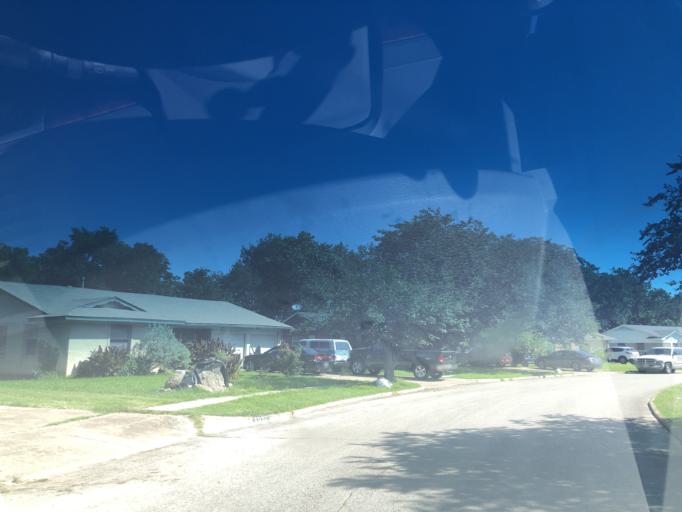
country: US
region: Texas
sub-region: Dallas County
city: Grand Prairie
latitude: 32.7151
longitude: -97.0117
